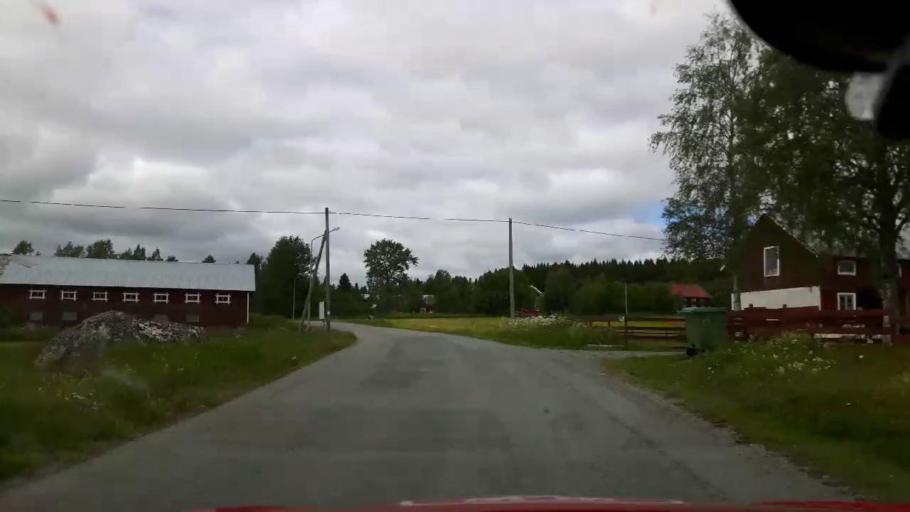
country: SE
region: Jaemtland
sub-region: OEstersunds Kommun
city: Brunflo
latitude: 63.0826
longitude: 14.8671
